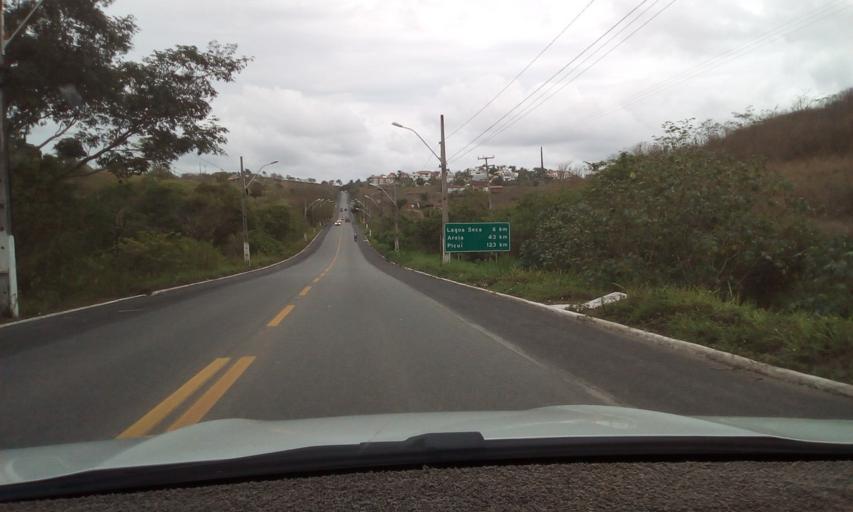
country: BR
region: Paraiba
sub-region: Lagoa Seca
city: Lagoa Seca
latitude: -7.1961
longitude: -35.8754
